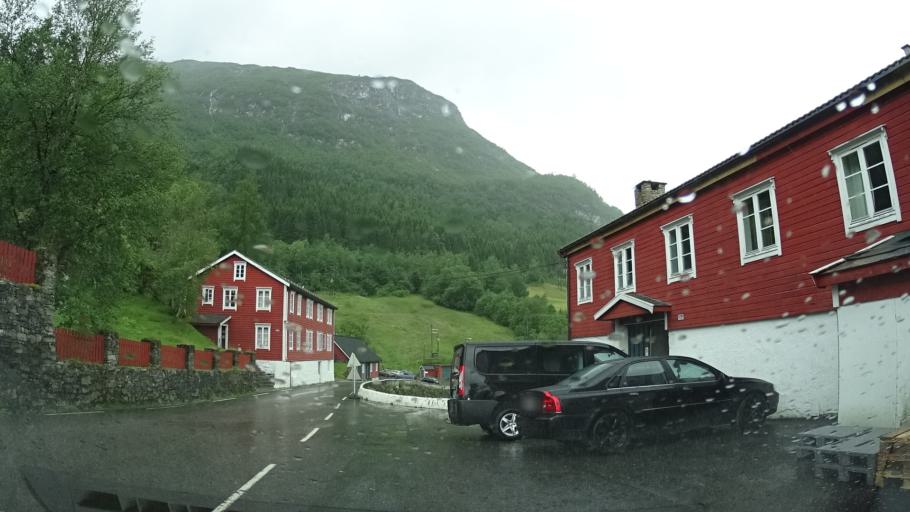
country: NO
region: Sogn og Fjordane
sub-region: Vik
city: Vik
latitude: 60.8352
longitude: 6.6808
